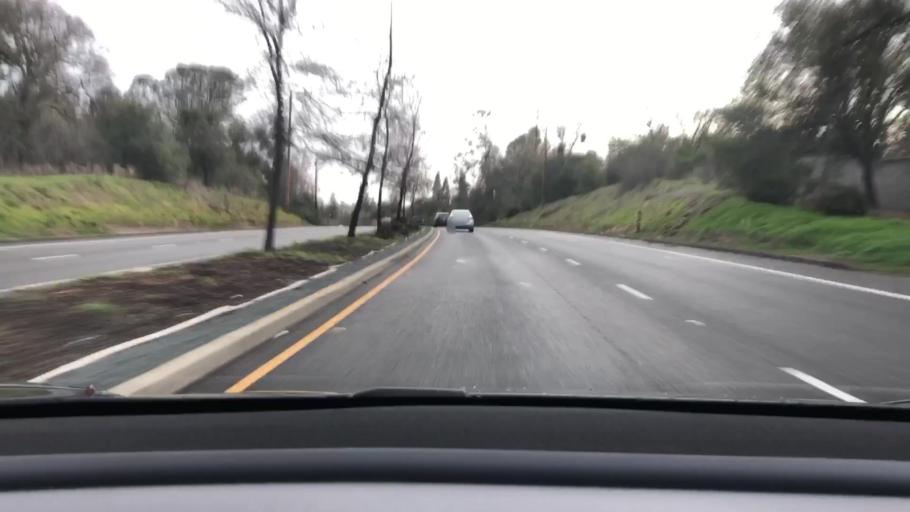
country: US
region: California
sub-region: Sacramento County
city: Folsom
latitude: 38.7171
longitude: -121.1759
